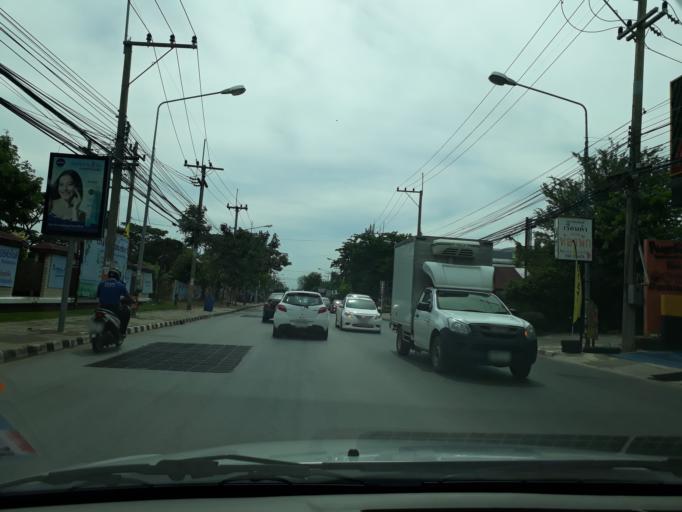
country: TH
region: Khon Kaen
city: Khon Kaen
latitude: 16.4372
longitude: 102.8438
